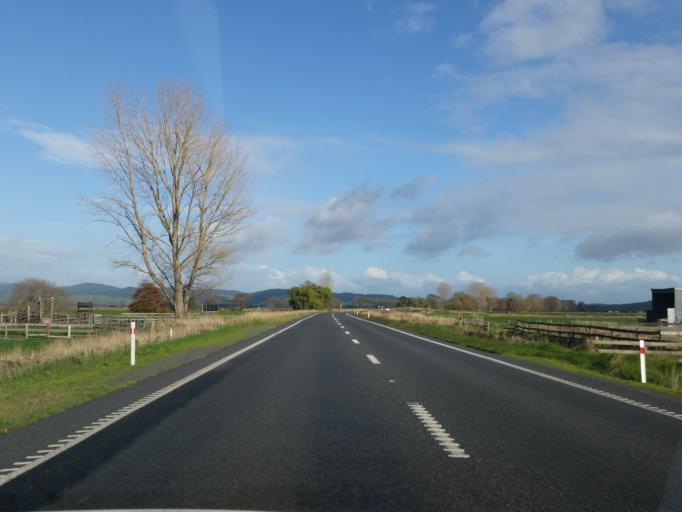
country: NZ
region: Waikato
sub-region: Hauraki District
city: Ngatea
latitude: -37.2772
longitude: 175.4611
